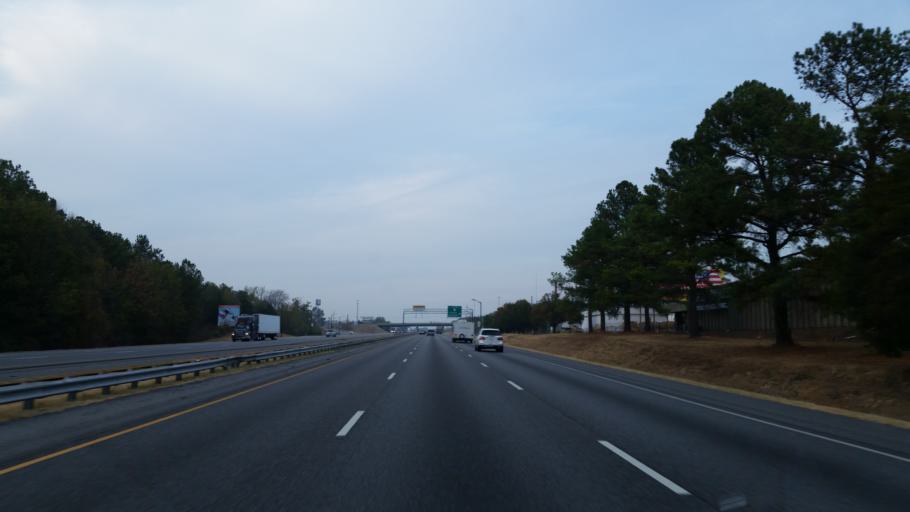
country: US
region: Georgia
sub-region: Gordon County
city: Calhoun
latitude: 34.4656
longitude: -84.9192
